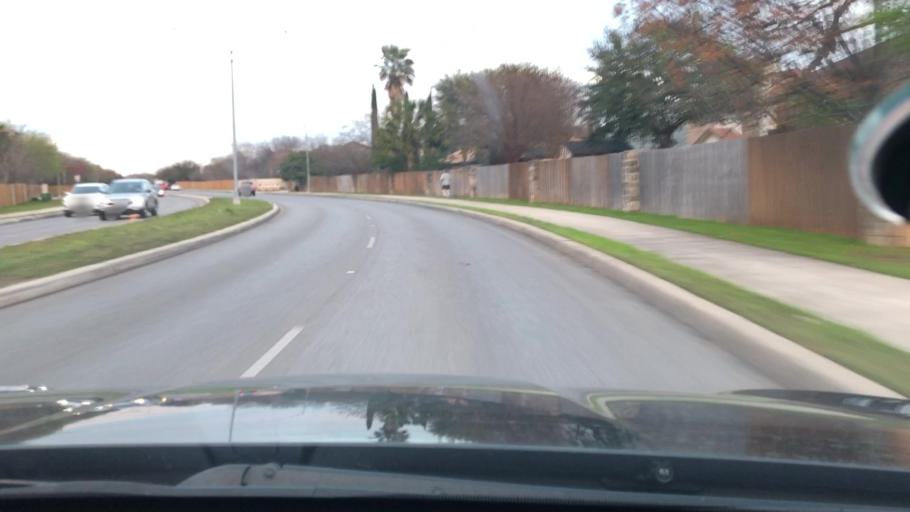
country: US
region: Texas
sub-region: Bexar County
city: Leon Valley
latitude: 29.5416
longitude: -98.6294
